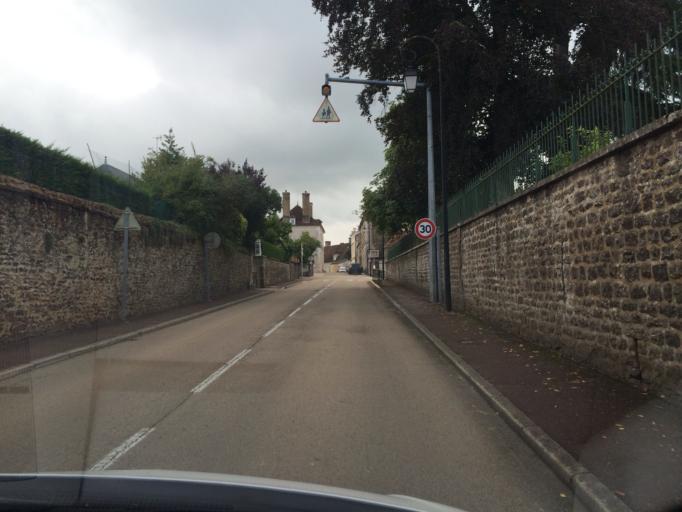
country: FR
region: Bourgogne
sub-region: Departement de l'Yonne
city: Saint-Fargeau
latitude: 47.6185
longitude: 3.1949
